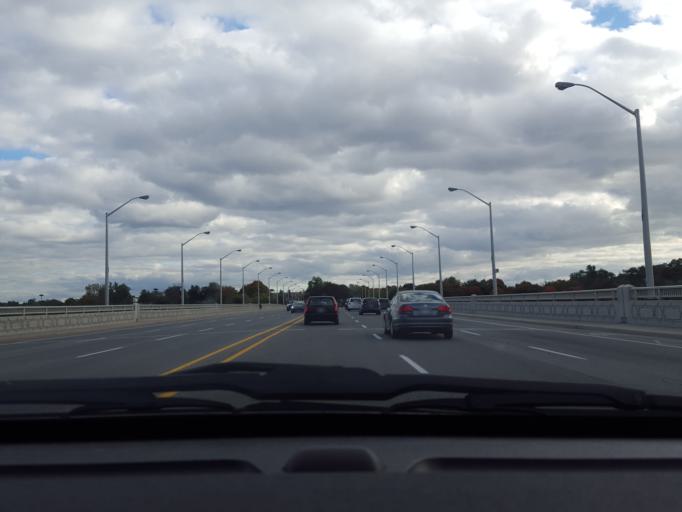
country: CA
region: Ontario
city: Toronto
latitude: 43.7006
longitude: -79.3512
